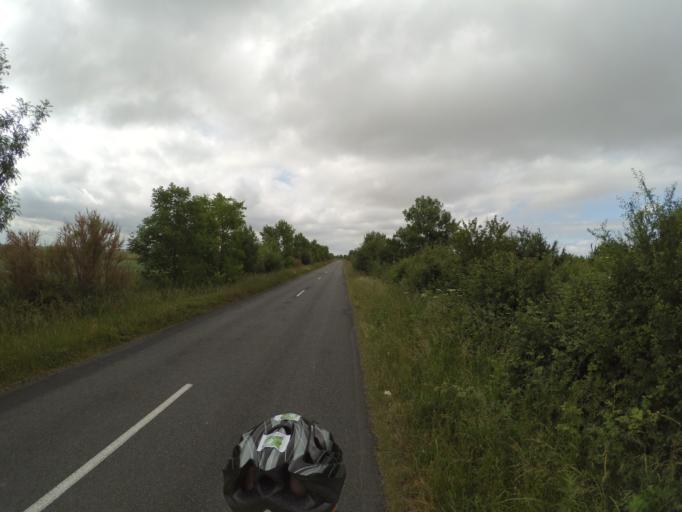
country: FR
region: Poitou-Charentes
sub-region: Departement de la Charente-Maritime
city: Yves
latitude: 46.0340
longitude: -1.0468
